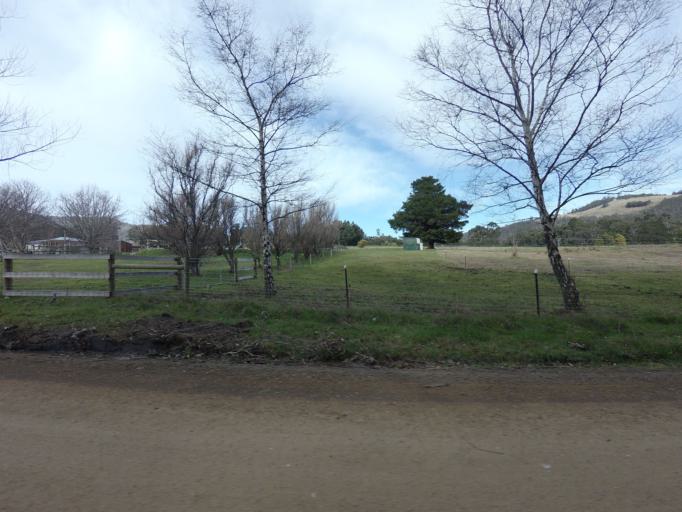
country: AU
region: Tasmania
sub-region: Huon Valley
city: Huonville
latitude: -43.0759
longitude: 147.0690
